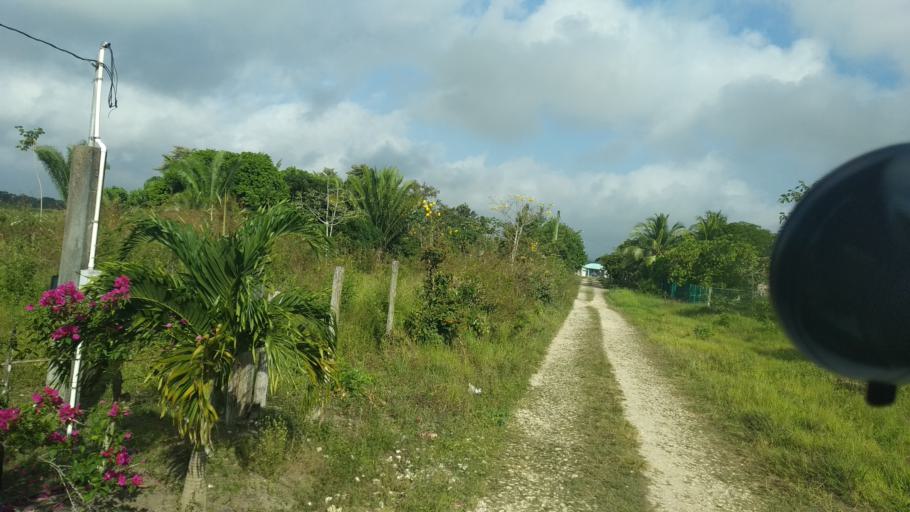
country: BZ
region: Stann Creek
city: Placencia
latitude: 16.5063
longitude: -88.5481
